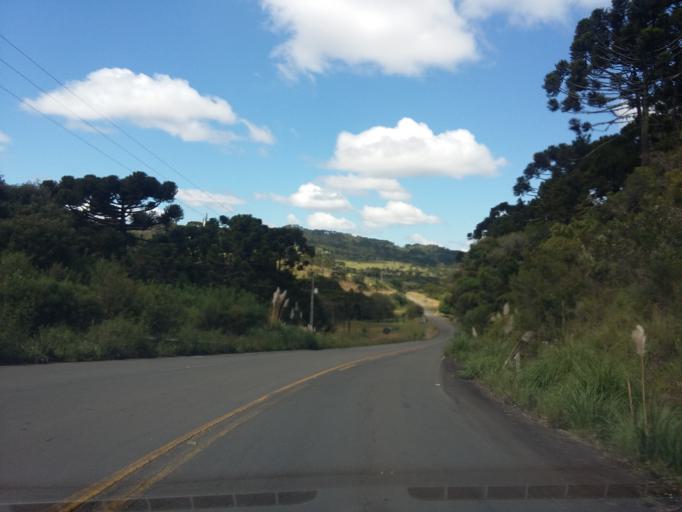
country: BR
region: Santa Catarina
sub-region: Sao Joaquim
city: Sao Joaquim
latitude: -28.2595
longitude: -49.7617
